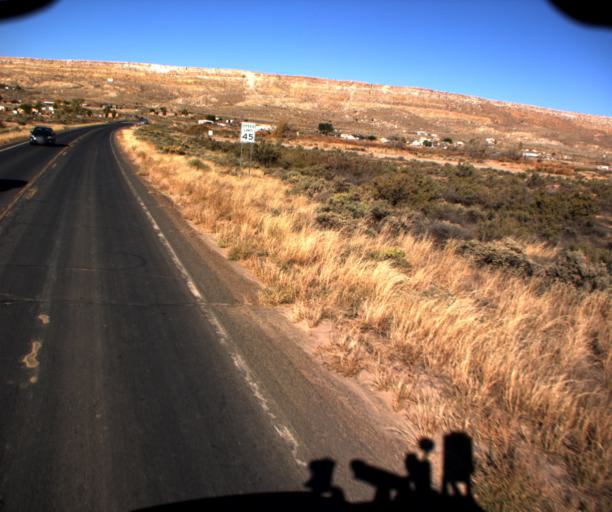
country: US
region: Arizona
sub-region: Navajo County
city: First Mesa
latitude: 35.8400
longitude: -110.3615
